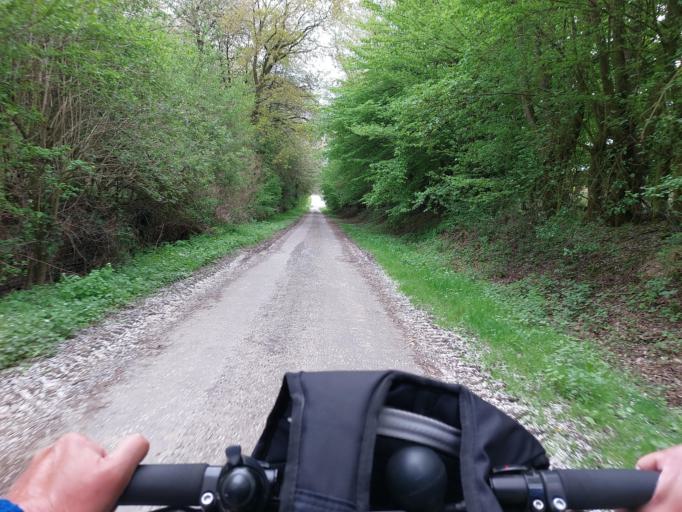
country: FR
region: Nord-Pas-de-Calais
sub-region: Departement du Nord
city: Bavay
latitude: 50.2939
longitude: 3.8161
